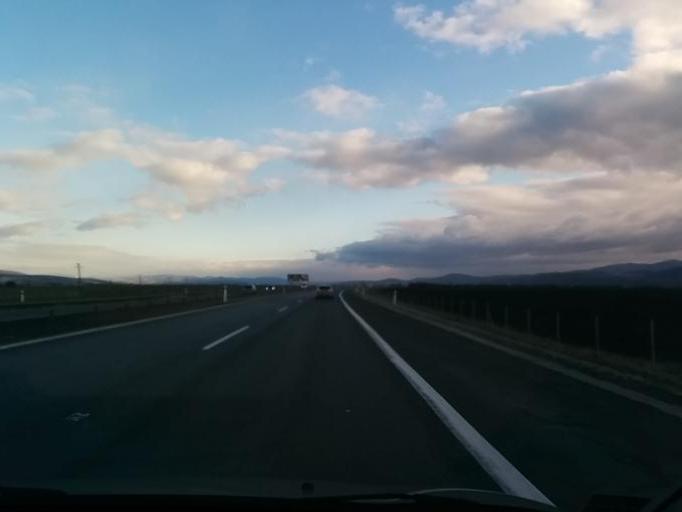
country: SK
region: Trnavsky
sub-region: Okres Trnava
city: Piestany
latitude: 48.6324
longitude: 17.8091
